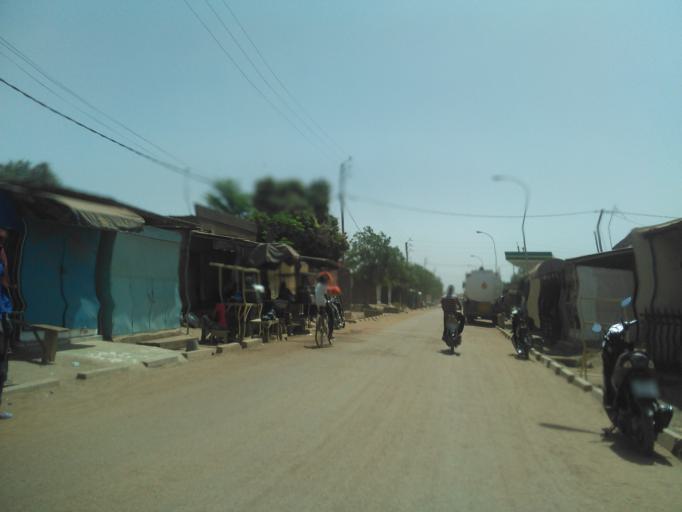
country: BF
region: Centre
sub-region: Kadiogo Province
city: Ouagadougou
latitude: 12.3927
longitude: -1.5633
